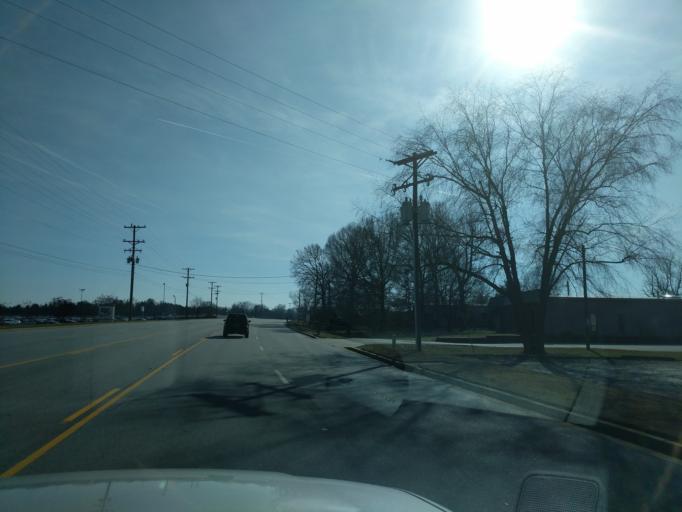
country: US
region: South Carolina
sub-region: Spartanburg County
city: Duncan
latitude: 34.8705
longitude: -82.1429
